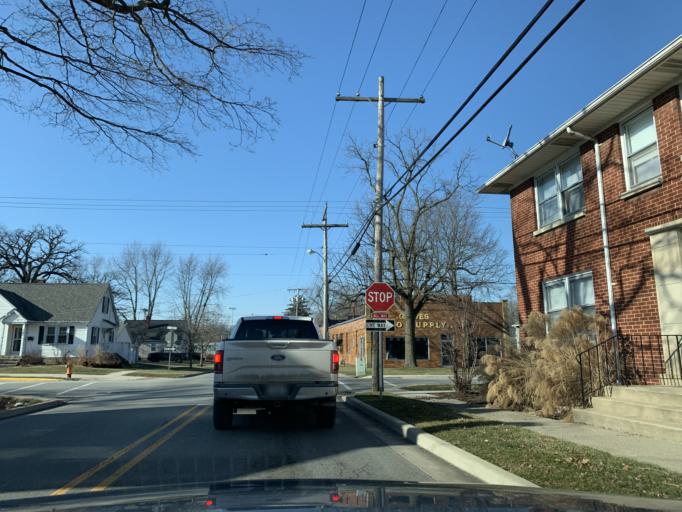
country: US
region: Indiana
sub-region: Lake County
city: Crown Point
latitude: 41.4203
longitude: -87.3652
